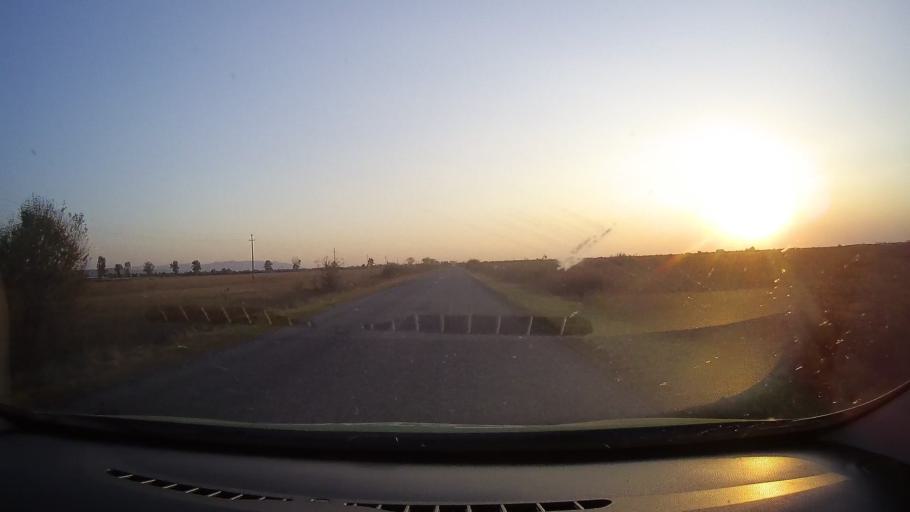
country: RO
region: Arad
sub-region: Comuna Seleus
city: Seleus
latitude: 46.3976
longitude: 21.7200
